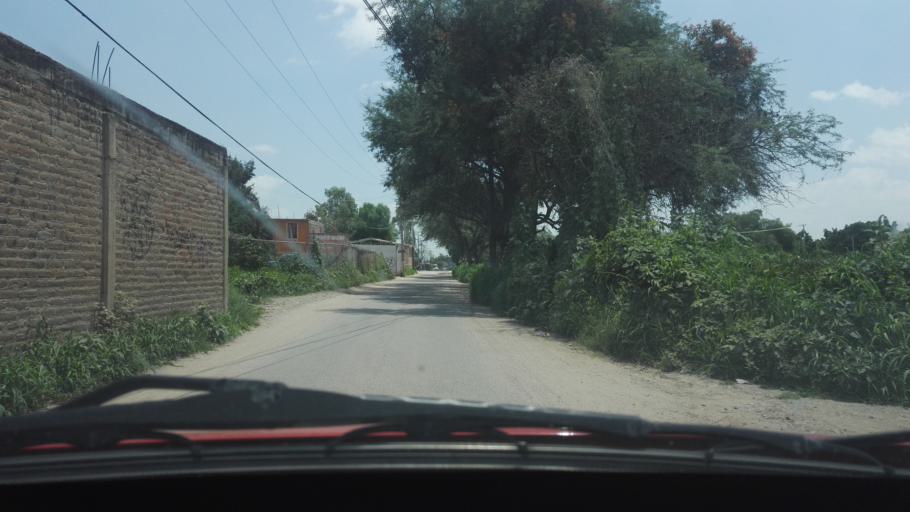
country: MX
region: Guanajuato
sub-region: Leon
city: Fraccionamiento Paraiso Real
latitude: 21.0751
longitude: -101.6093
